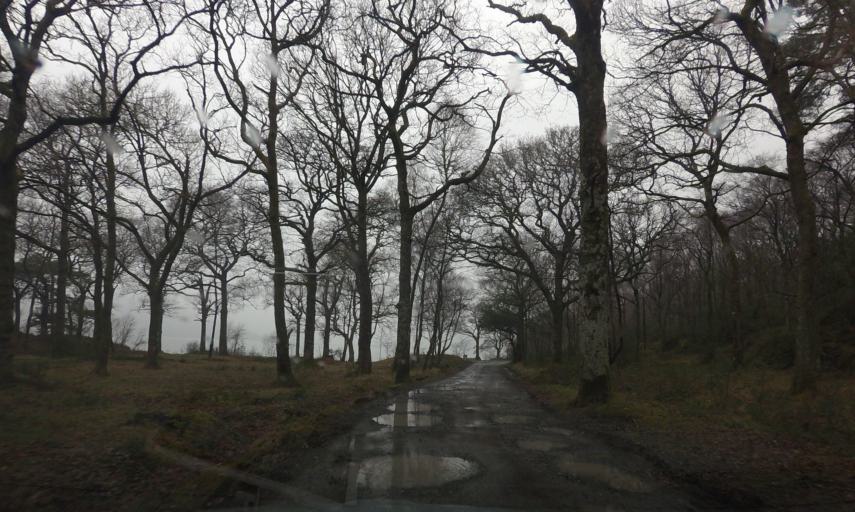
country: GB
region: Scotland
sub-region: West Dunbartonshire
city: Balloch
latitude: 56.1531
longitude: -4.6419
